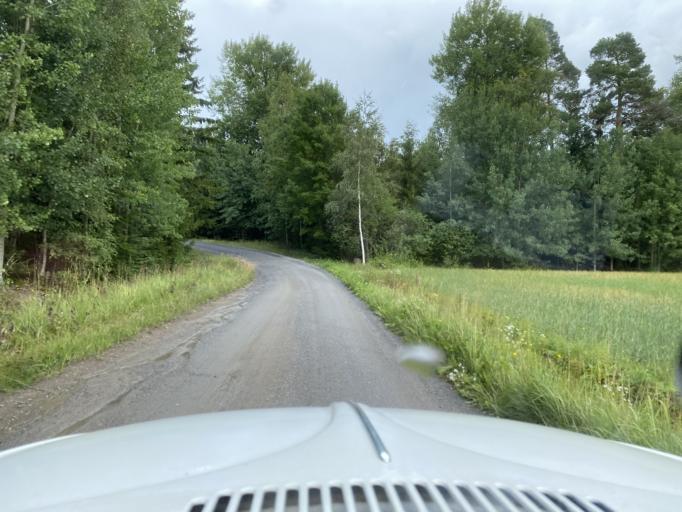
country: FI
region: Pirkanmaa
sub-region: Lounais-Pirkanmaa
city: Punkalaidun
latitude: 61.1268
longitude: 23.0641
